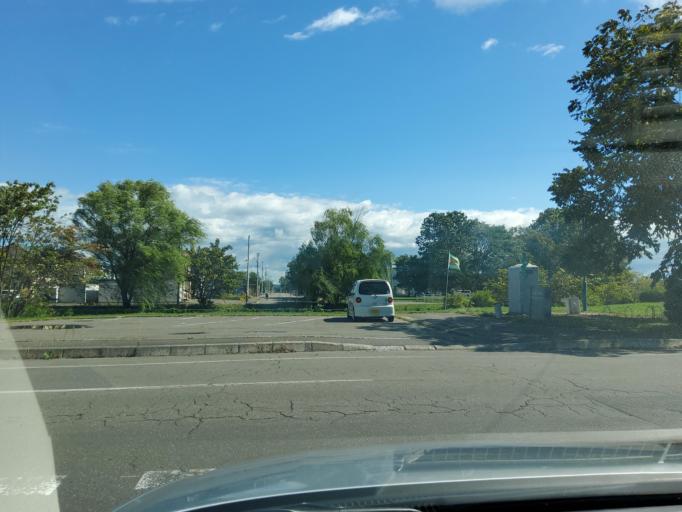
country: JP
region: Hokkaido
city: Otofuke
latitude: 42.9589
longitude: 143.1936
